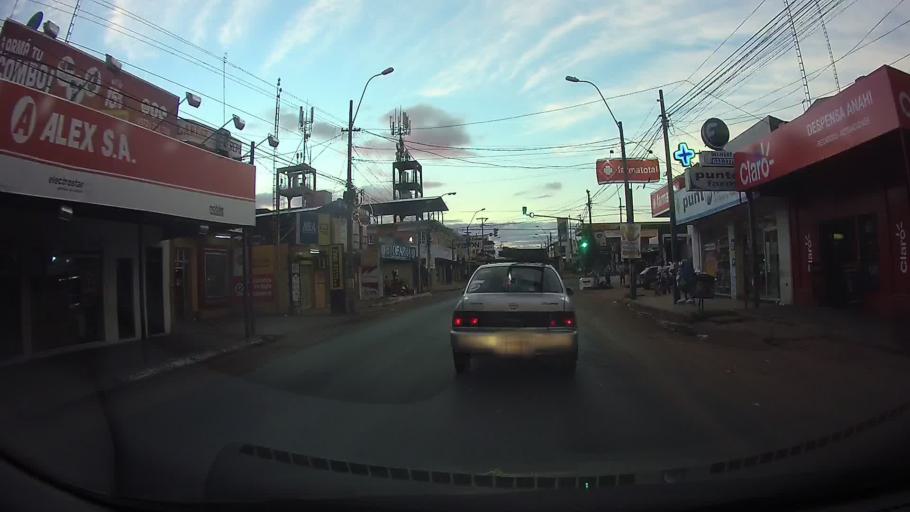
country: PY
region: Central
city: Ita
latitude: -25.5075
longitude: -57.3573
